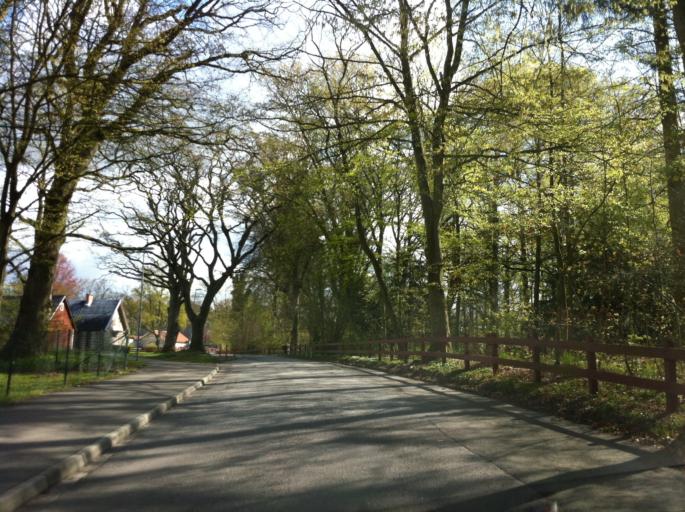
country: SE
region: Skane
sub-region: Hoors Kommun
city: Satofta
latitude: 55.9022
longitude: 13.5340
